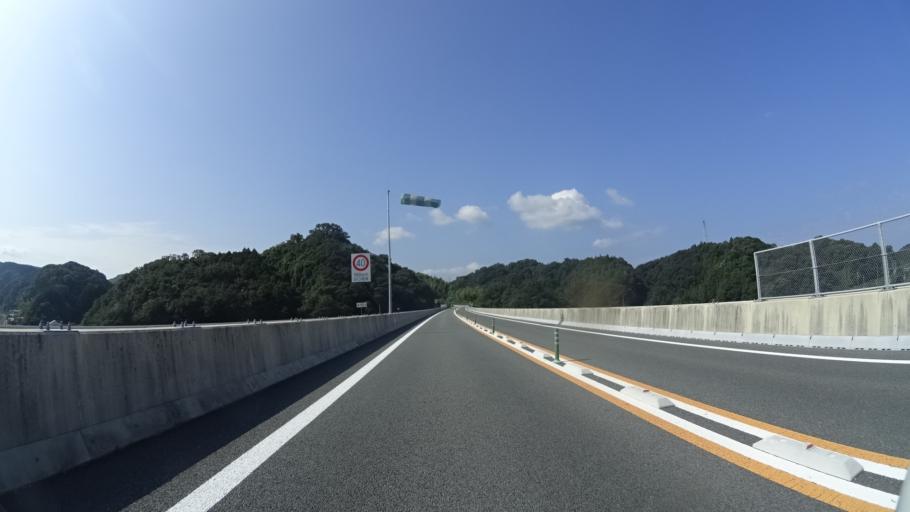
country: JP
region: Shimane
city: Gotsucho
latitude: 35.0729
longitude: 132.3319
